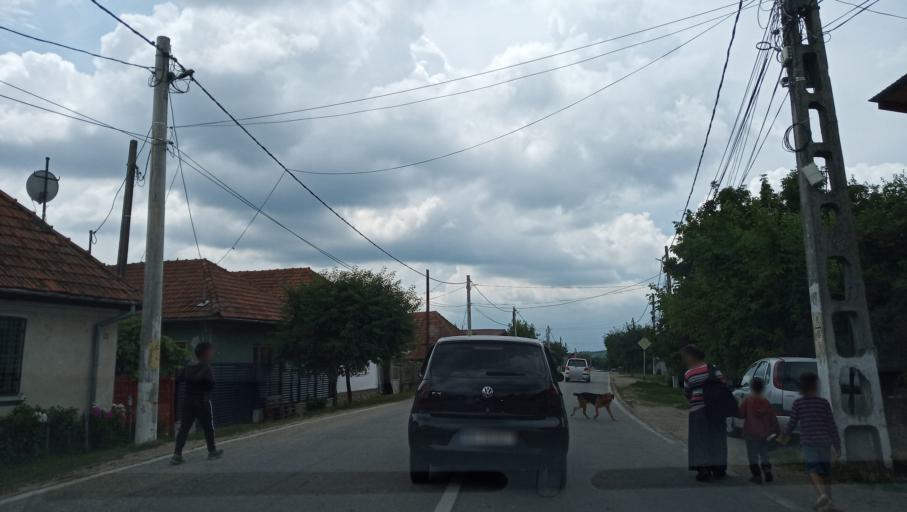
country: RO
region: Gorj
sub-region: Comuna Pestisani
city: Pestisani
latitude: 45.0774
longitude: 23.0452
